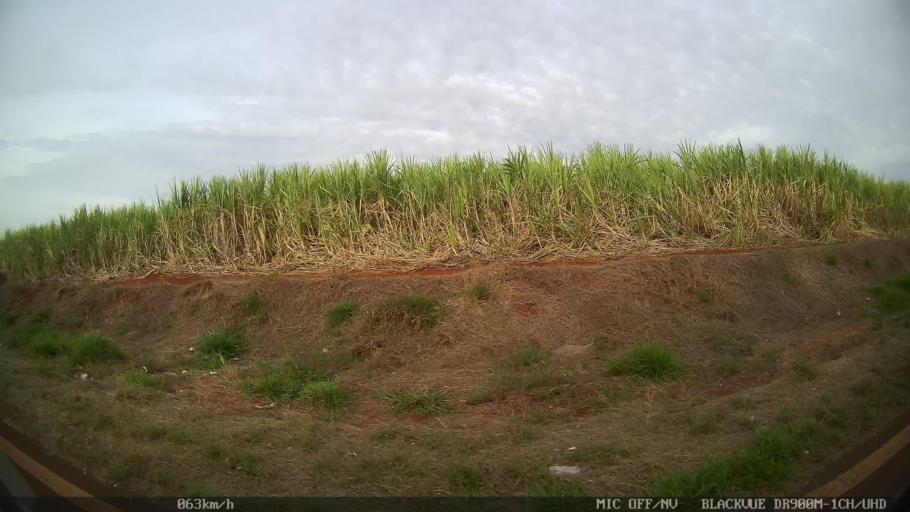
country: BR
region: Sao Paulo
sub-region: Piracicaba
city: Piracicaba
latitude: -22.7163
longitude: -47.5818
